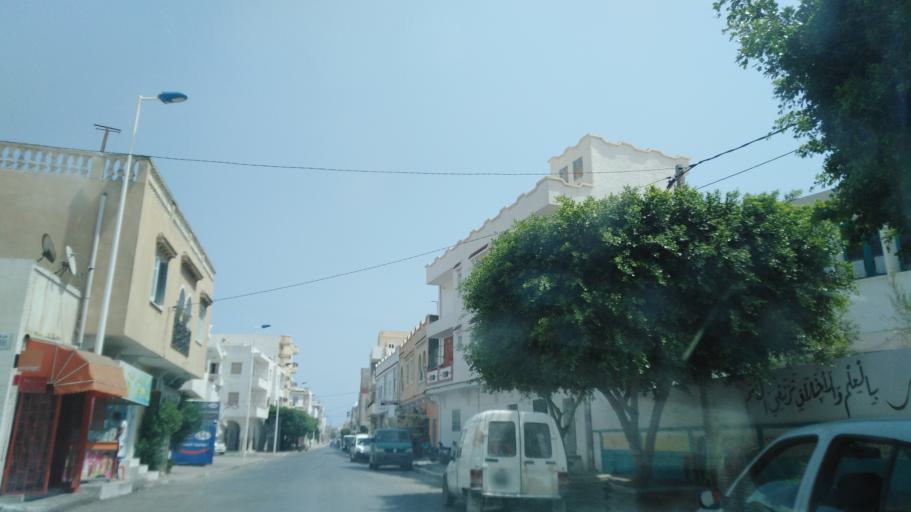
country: TN
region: Al Mahdiyah
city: Mahdia
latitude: 35.5130
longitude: 11.0455
